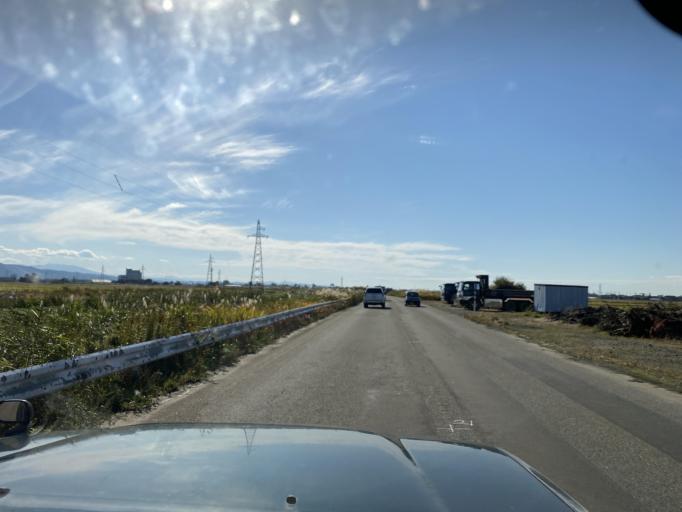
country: JP
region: Niigata
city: Niitsu-honcho
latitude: 37.8039
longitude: 139.0781
